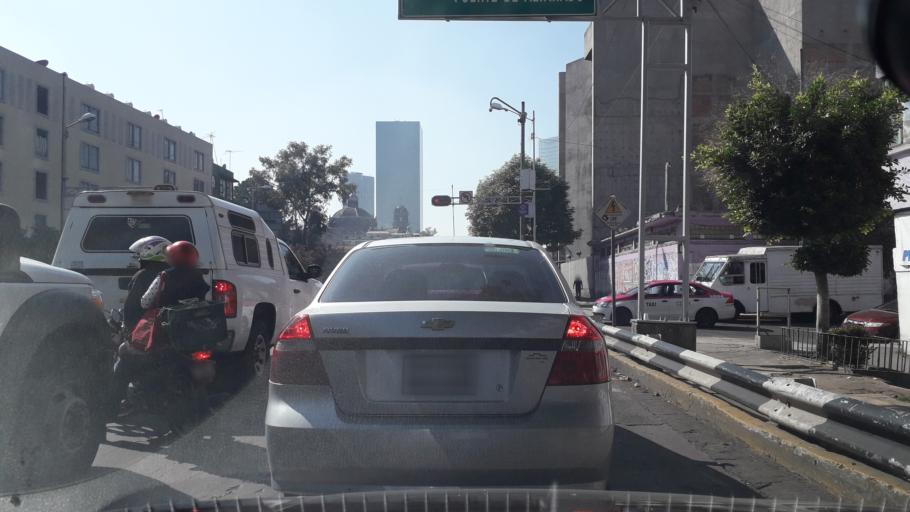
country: MX
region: Mexico City
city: Cuauhtemoc
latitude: 19.4419
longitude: -99.1483
